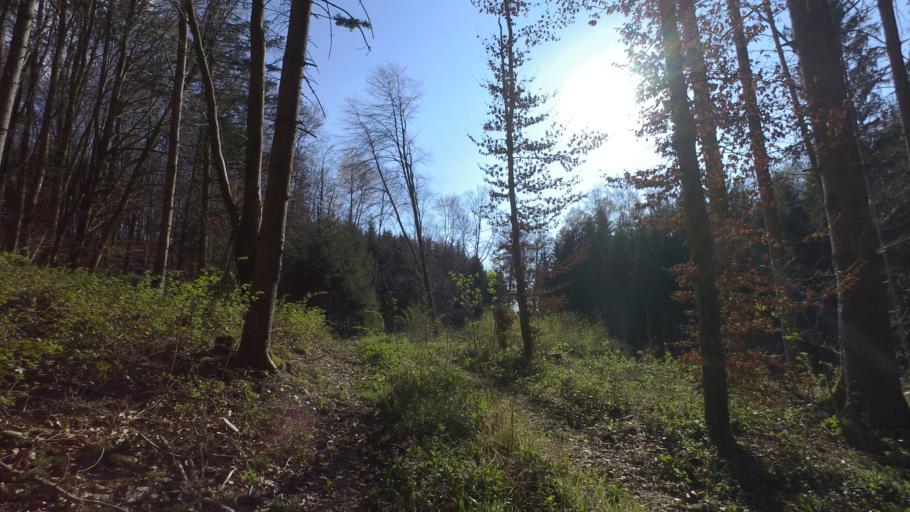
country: DE
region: Bavaria
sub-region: Upper Bavaria
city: Nussdorf
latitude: 47.9249
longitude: 12.5766
